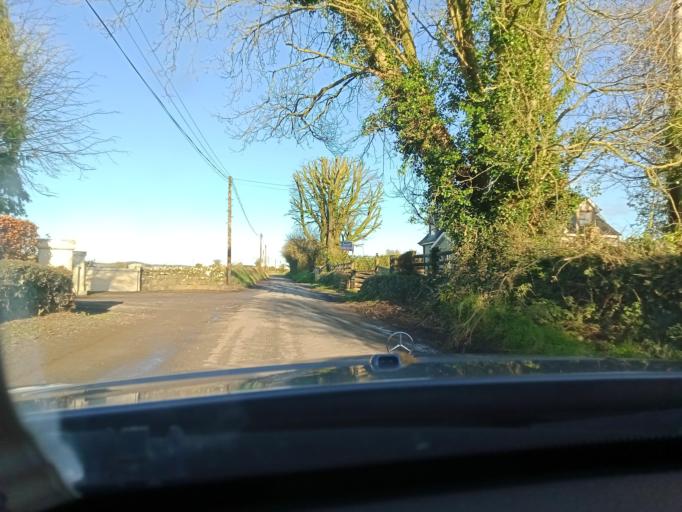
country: IE
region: Leinster
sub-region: Kilkenny
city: Mooncoin
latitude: 52.2858
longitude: -7.2355
